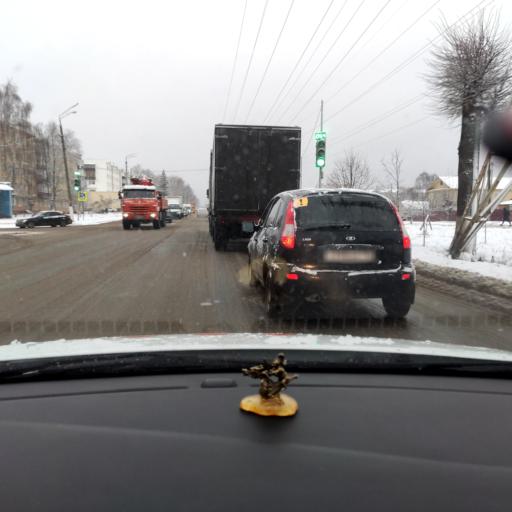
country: RU
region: Tatarstan
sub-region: Zelenodol'skiy Rayon
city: Zelenodolsk
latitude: 55.8515
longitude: 48.5259
